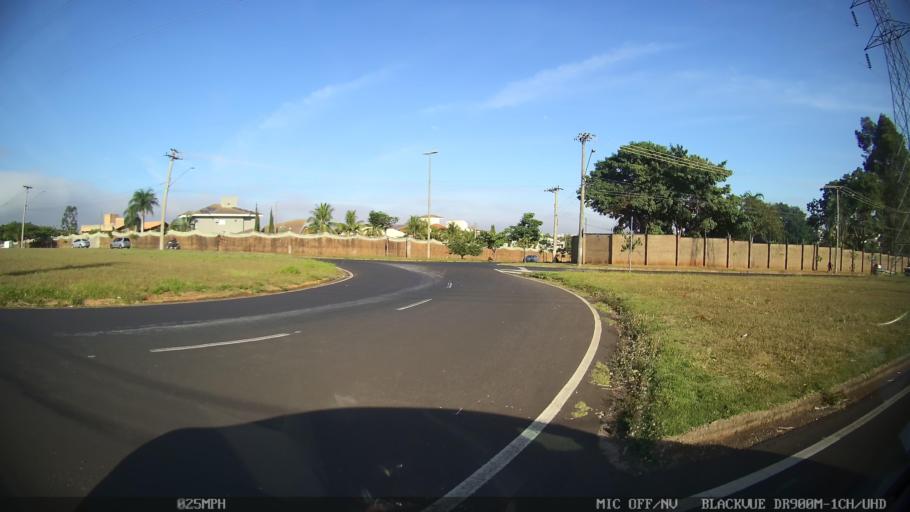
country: BR
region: Sao Paulo
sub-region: Sao Jose Do Rio Preto
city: Sao Jose do Rio Preto
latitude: -20.8086
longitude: -49.3420
